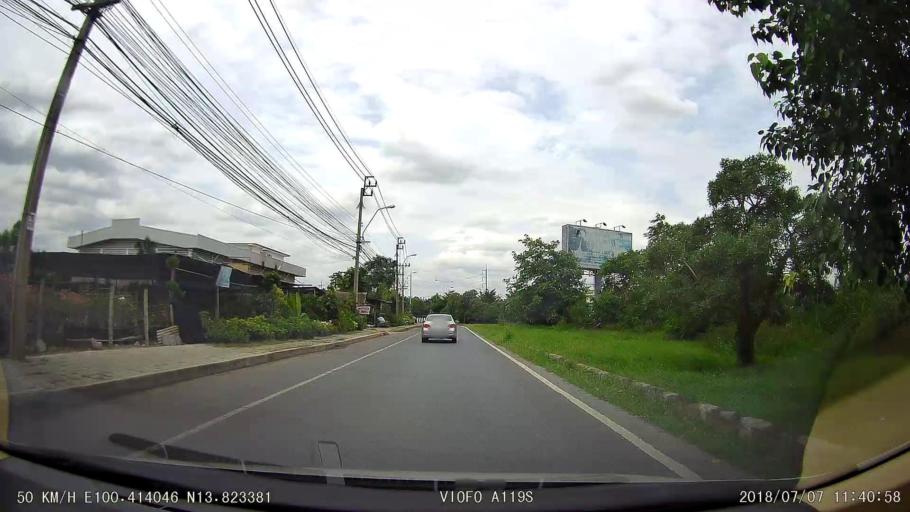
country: TH
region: Nonthaburi
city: Bang Yai
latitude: 13.8234
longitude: 100.4141
